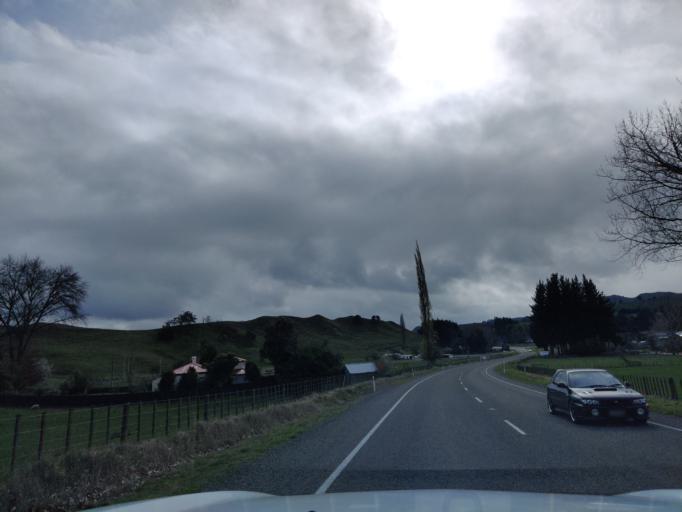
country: NZ
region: Manawatu-Wanganui
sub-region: Ruapehu District
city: Waiouru
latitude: -39.7378
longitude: 175.8405
